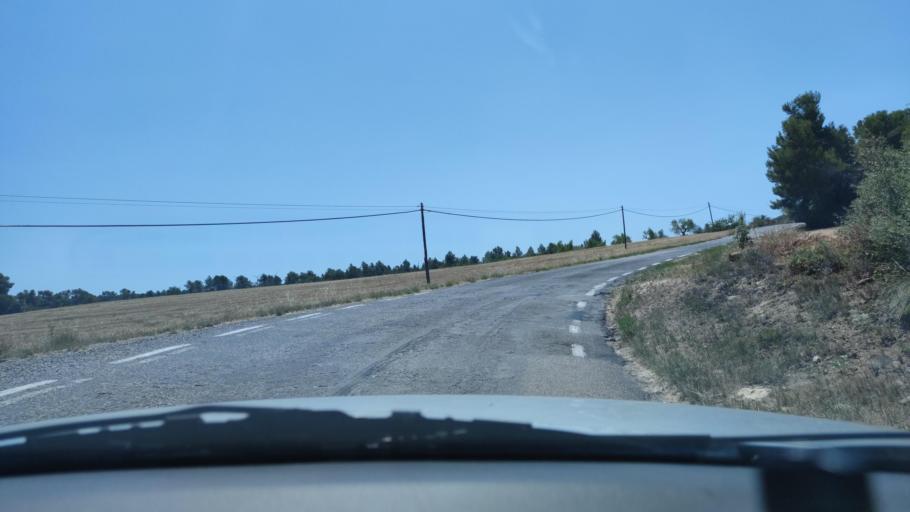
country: ES
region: Catalonia
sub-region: Provincia de Lleida
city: Fulleda
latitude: 41.4752
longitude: 1.0215
